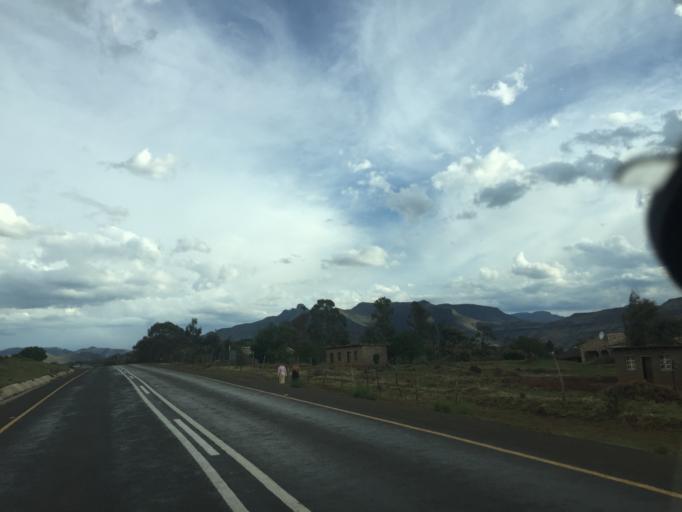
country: LS
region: Berea
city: Teyateyaneng
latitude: -29.1469
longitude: 28.0041
